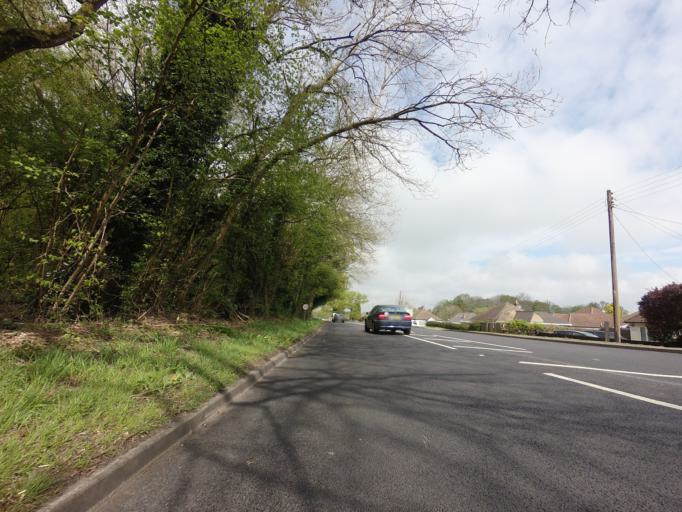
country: GB
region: England
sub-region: Kent
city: Borough Green
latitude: 51.3296
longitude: 0.2838
